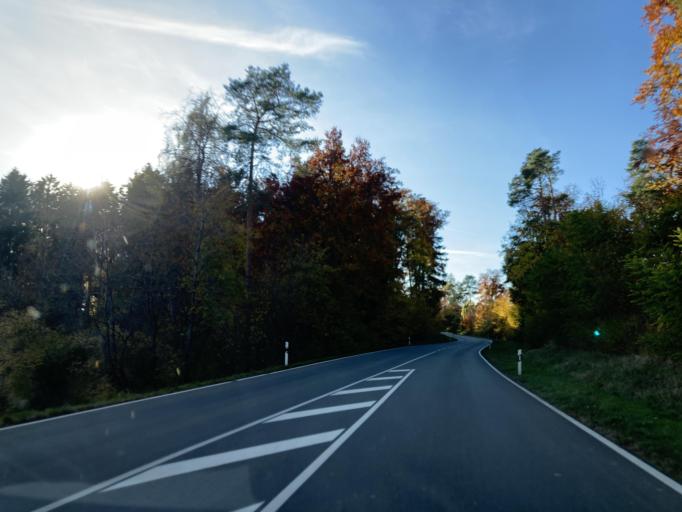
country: DE
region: Baden-Wuerttemberg
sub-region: Karlsruhe Region
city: Horb am Neckar
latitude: 48.4522
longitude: 8.6545
